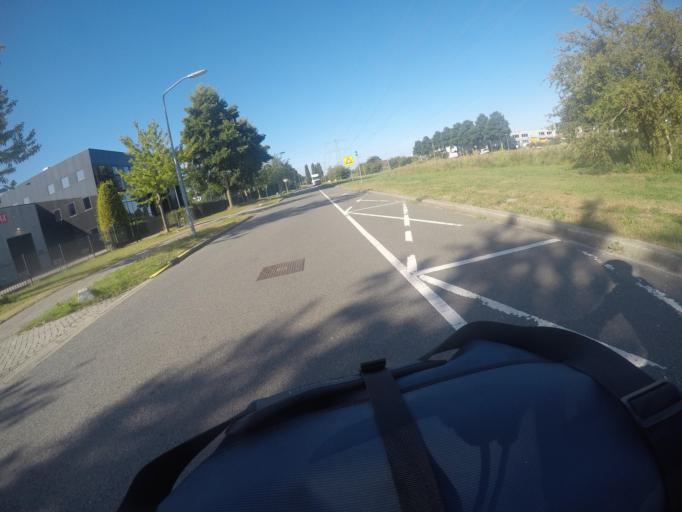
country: NL
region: Flevoland
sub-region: Gemeente Almere
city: Almere Stad
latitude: 52.3503
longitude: 5.1880
